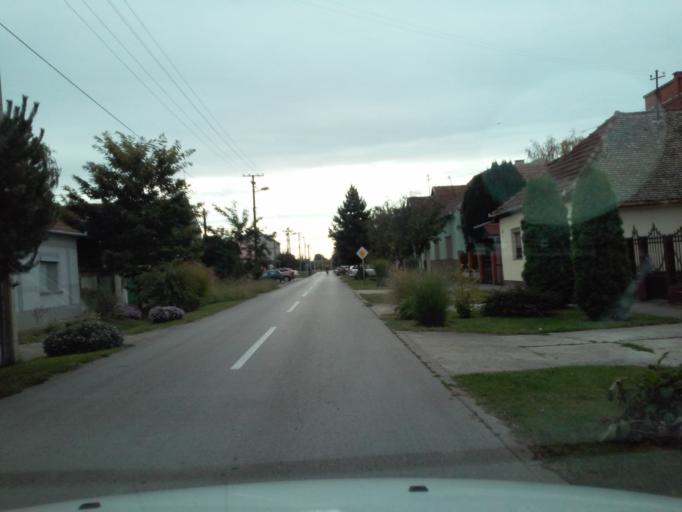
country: RS
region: Autonomna Pokrajina Vojvodina
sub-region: Severnobanatski Okrug
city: Kikinda
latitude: 45.8230
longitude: 20.4698
